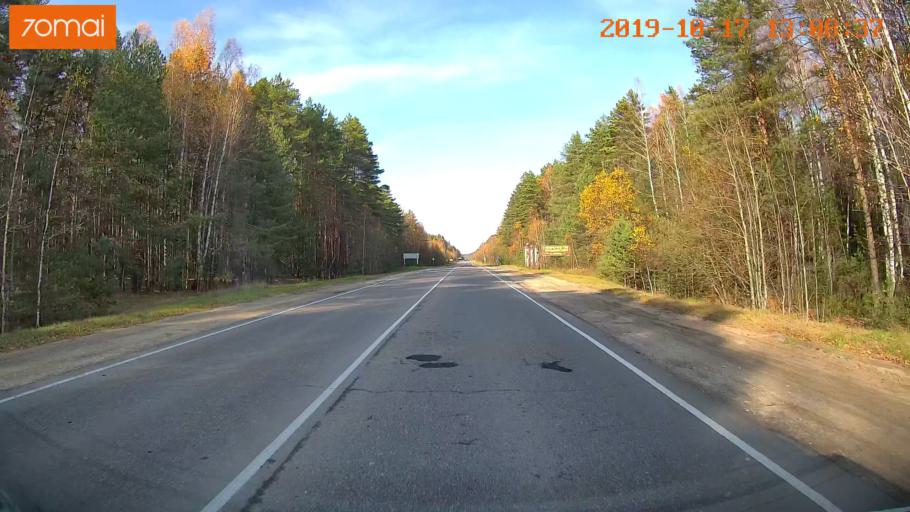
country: RU
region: Rjazan
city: Syntul
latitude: 54.9914
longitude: 41.2681
